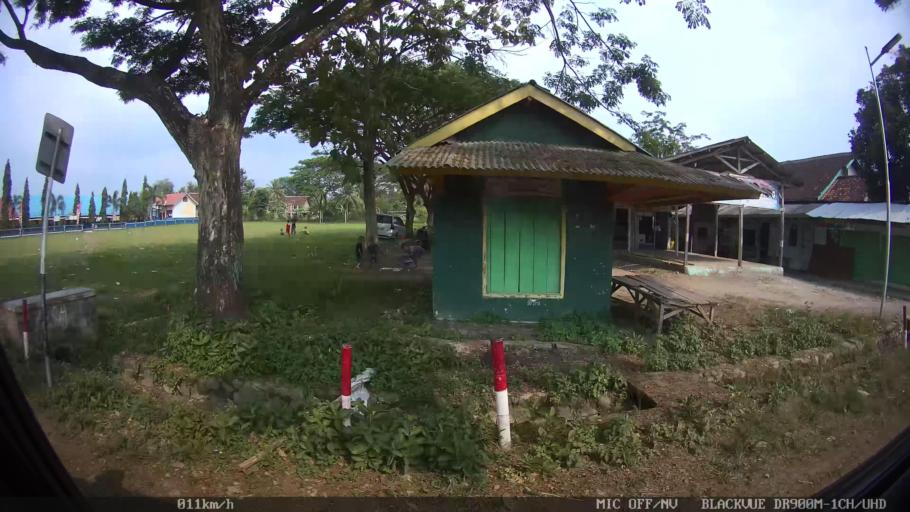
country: ID
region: Lampung
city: Gadingrejo
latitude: -5.4007
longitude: 105.0244
